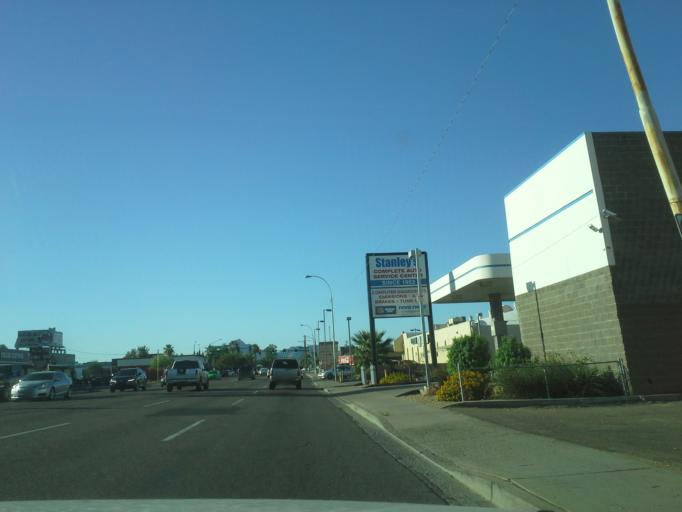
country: US
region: Arizona
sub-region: Maricopa County
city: Phoenix
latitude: 33.4640
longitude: -112.0128
